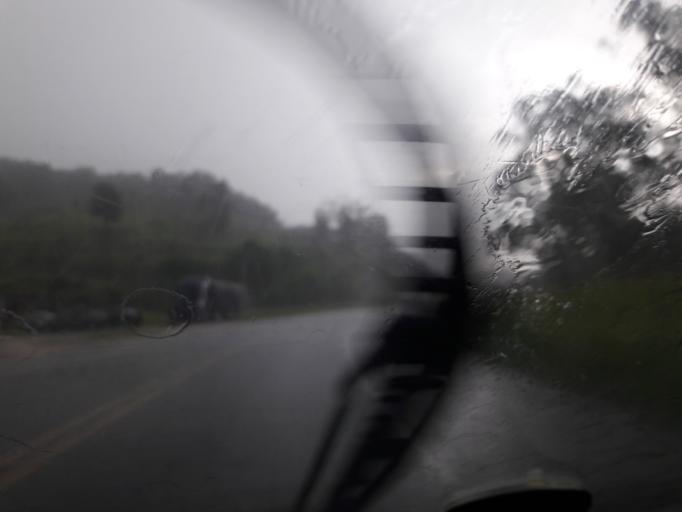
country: BR
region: Sao Paulo
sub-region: Bom Jesus Dos Perdoes
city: Bom Jesus dos Perdoes
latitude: -23.1783
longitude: -46.3974
